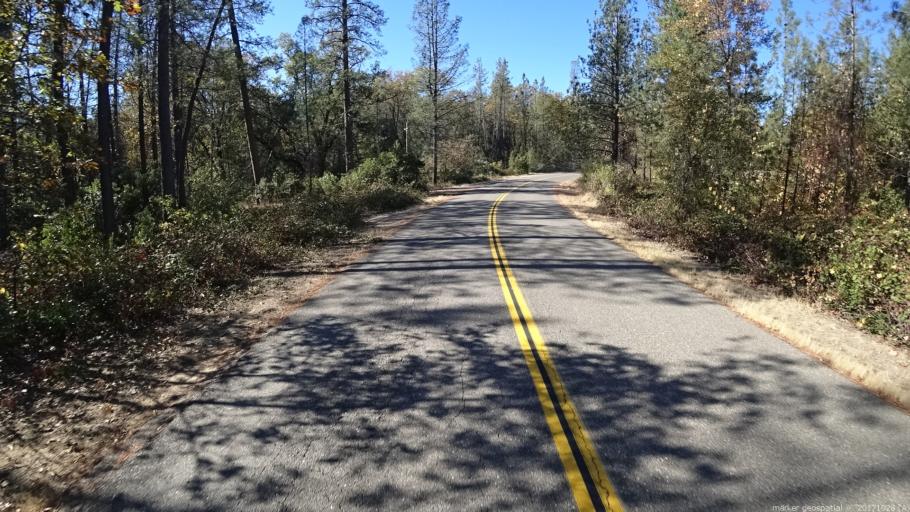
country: US
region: California
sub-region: Shasta County
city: Shasta
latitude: 40.5850
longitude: -122.5389
